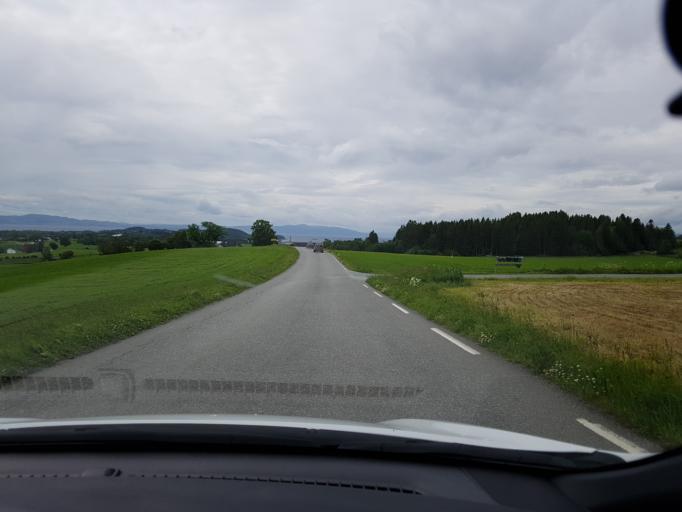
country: NO
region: Nord-Trondelag
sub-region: Frosta
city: Frosta
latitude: 63.5798
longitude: 10.7157
